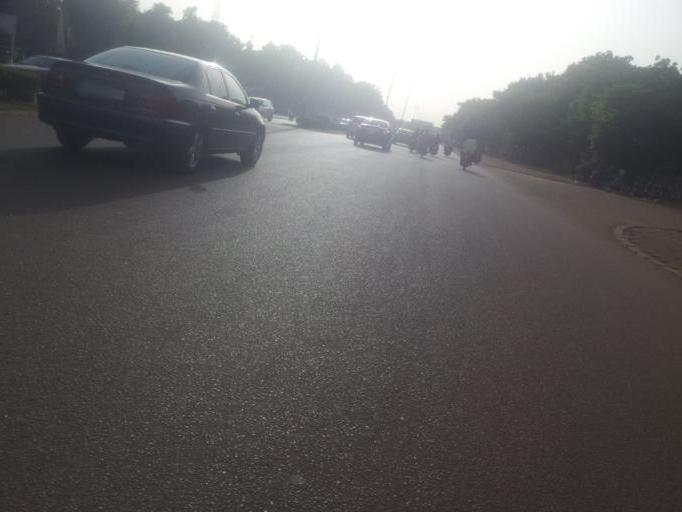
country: BF
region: Centre
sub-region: Kadiogo Province
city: Ouagadougou
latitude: 12.3725
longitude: -1.5143
